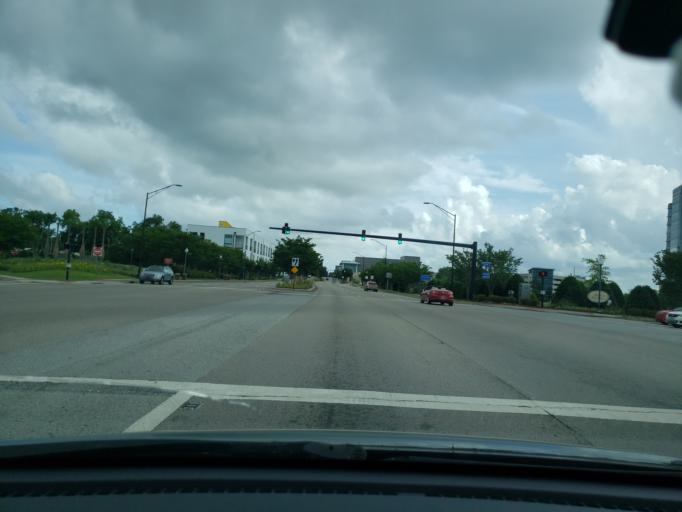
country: US
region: North Carolina
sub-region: New Hanover County
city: Wilmington
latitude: 34.2486
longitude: -77.9477
